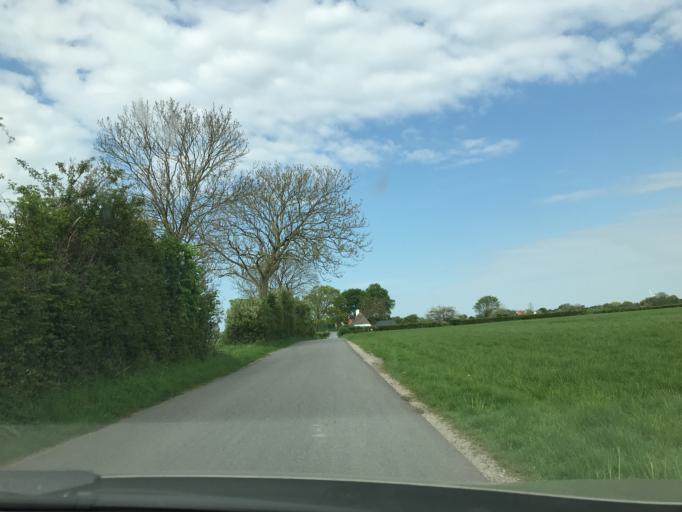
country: DK
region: South Denmark
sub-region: Middelfart Kommune
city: Norre Aby
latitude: 55.3673
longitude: 9.8392
